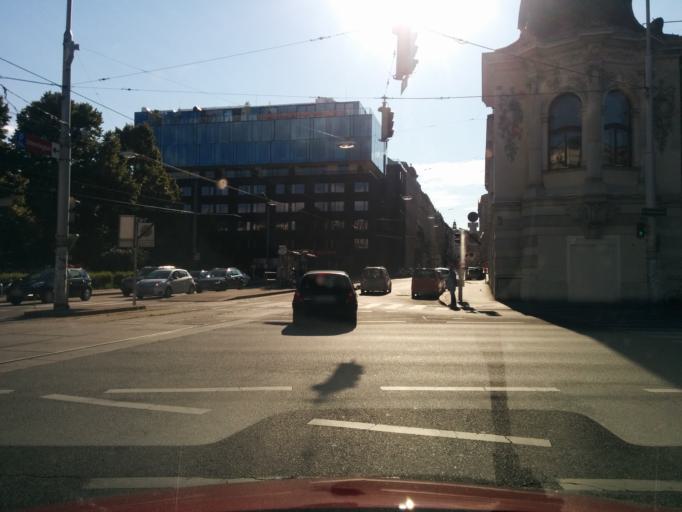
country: AT
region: Vienna
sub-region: Wien Stadt
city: Vienna
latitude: 48.2069
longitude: 16.3558
